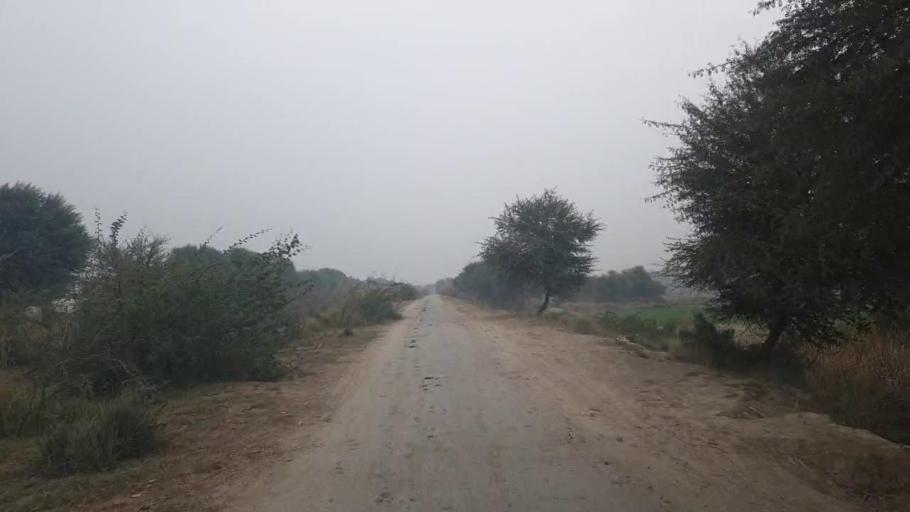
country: PK
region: Sindh
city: Tando Adam
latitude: 25.7498
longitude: 68.7027
